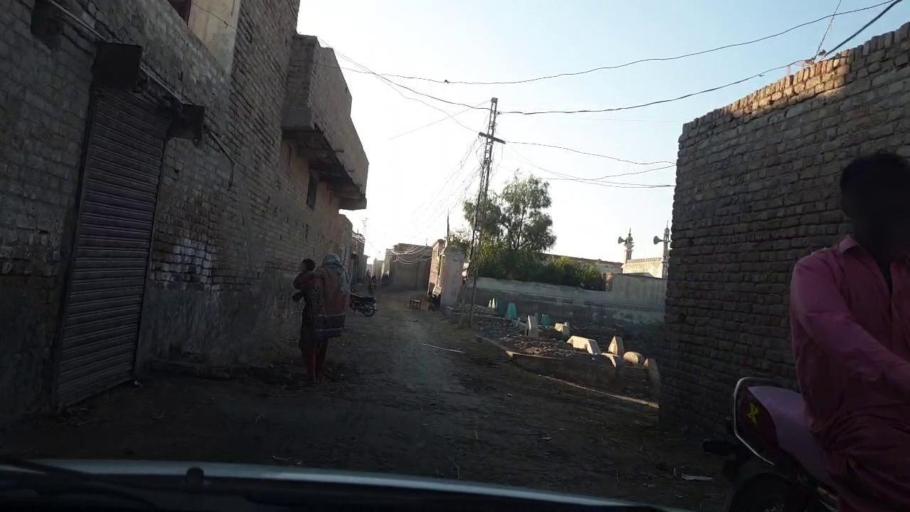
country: PK
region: Sindh
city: Khairpur Nathan Shah
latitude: 27.0709
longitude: 67.7244
